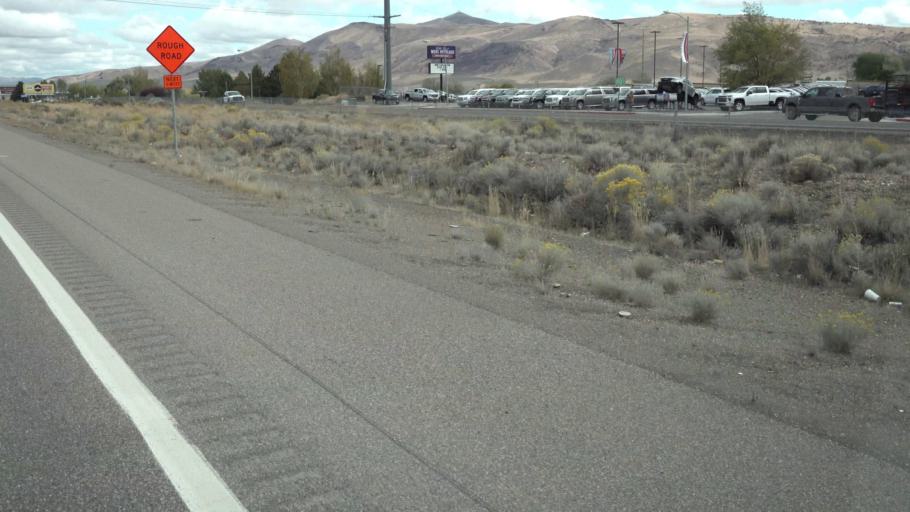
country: US
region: Nevada
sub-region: Elko County
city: Elko
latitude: 40.8611
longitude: -115.7372
